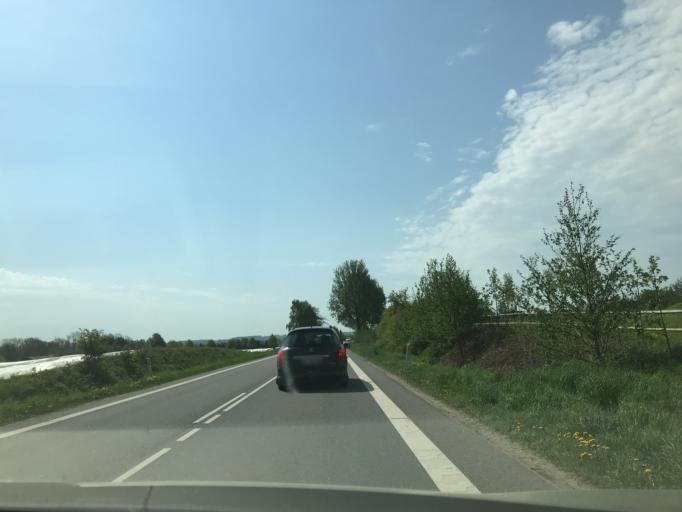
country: DK
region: South Denmark
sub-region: Assens Kommune
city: Assens
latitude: 55.3371
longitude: 9.9386
